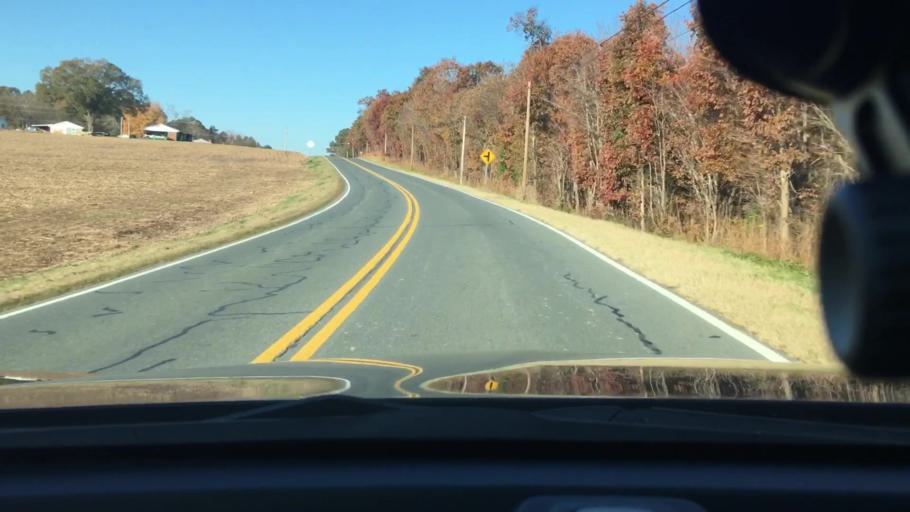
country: US
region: North Carolina
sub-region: Cabarrus County
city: Mount Pleasant
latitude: 35.3845
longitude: -80.3284
